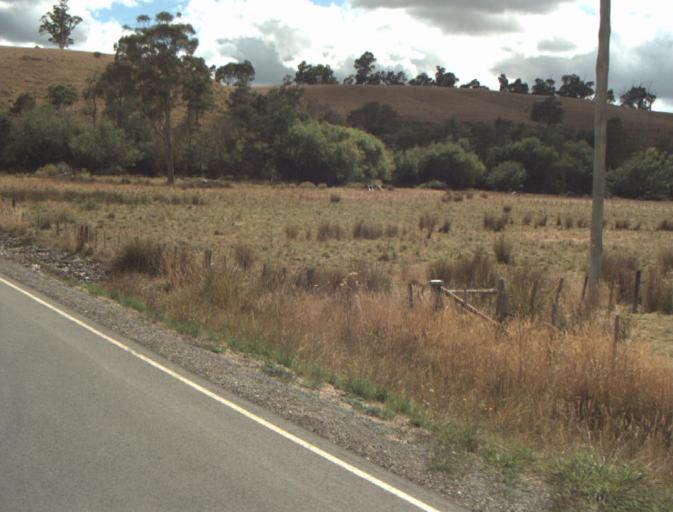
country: AU
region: Tasmania
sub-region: Launceston
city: Mayfield
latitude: -41.2212
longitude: 147.1372
